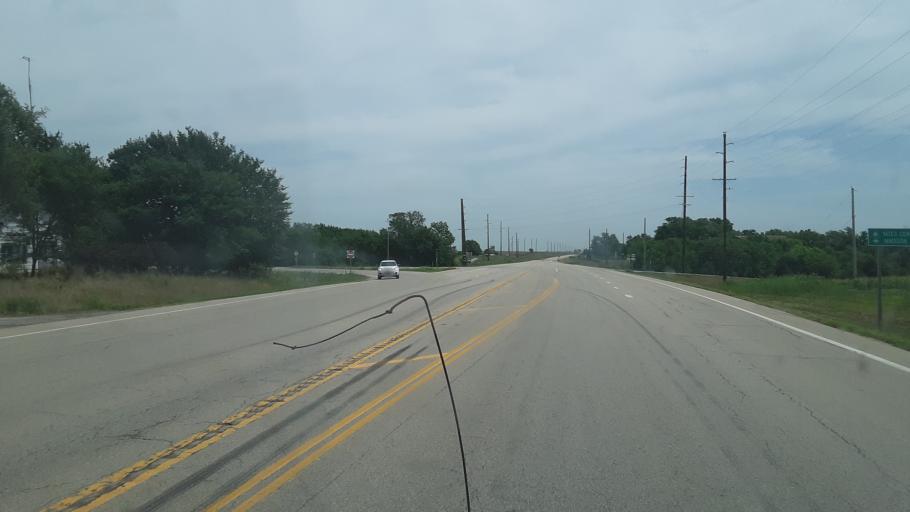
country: US
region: Kansas
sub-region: Greenwood County
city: Eureka
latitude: 37.8387
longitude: -96.1791
